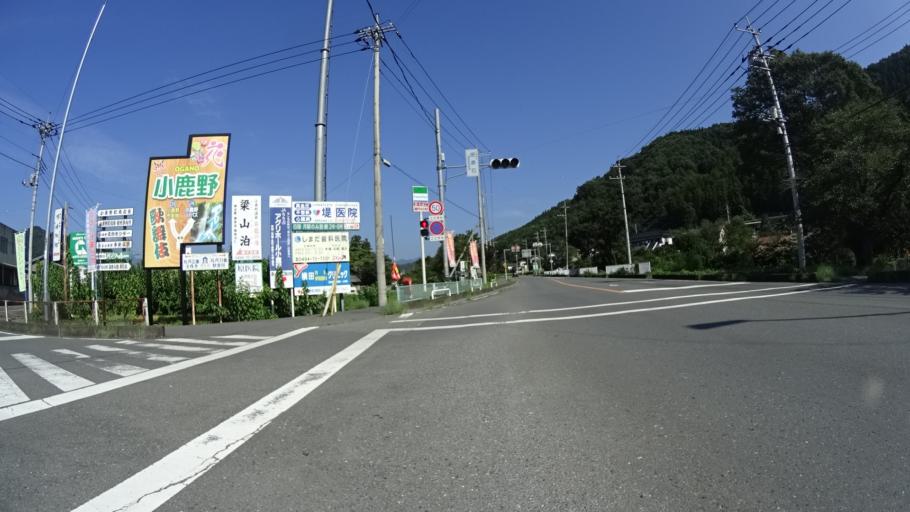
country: JP
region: Saitama
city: Chichibu
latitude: 36.0135
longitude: 139.0212
